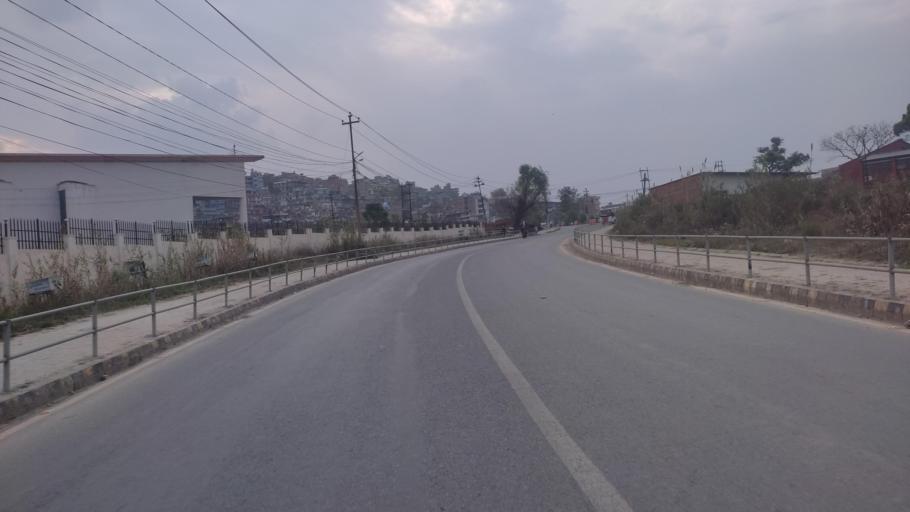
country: NP
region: Central Region
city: Kirtipur
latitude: 27.6760
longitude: 85.2847
